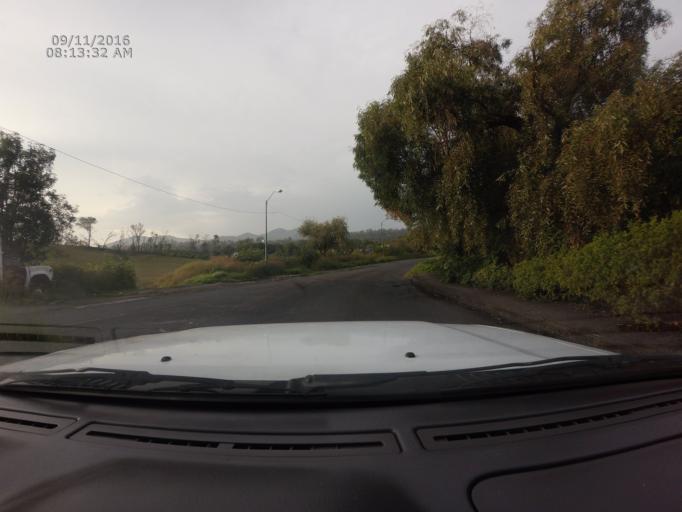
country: MX
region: Michoacan
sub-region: Morelia
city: Morelos
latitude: 19.6646
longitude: -101.2253
